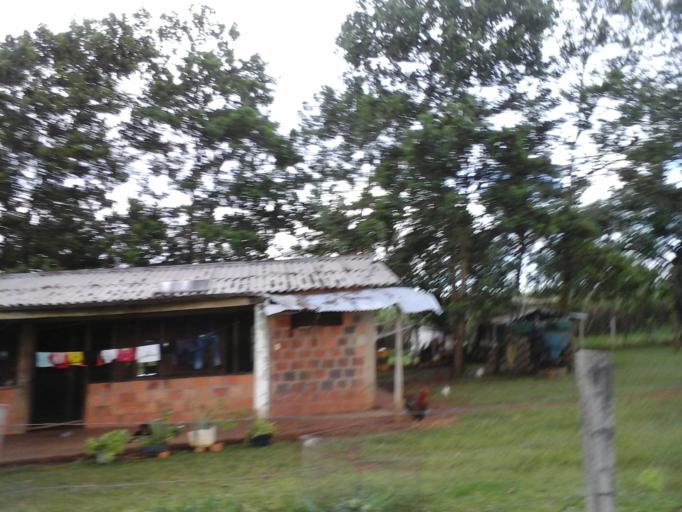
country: CO
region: Cundinamarca
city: Tibacuy
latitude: 4.1926
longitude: -72.4319
